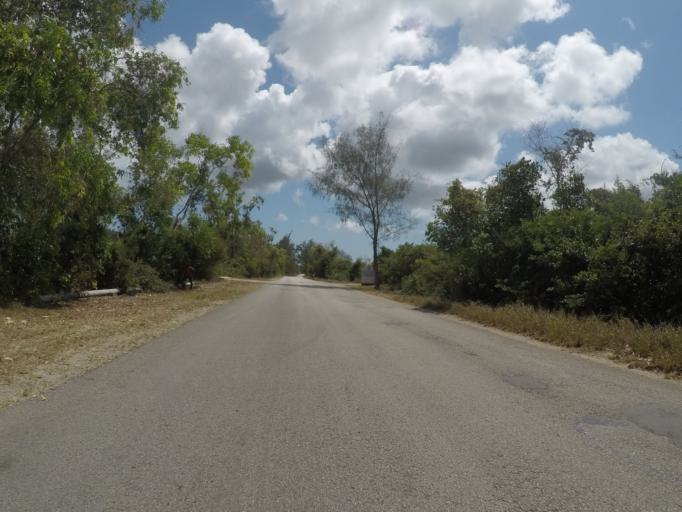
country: TZ
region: Zanzibar Central/South
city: Nganane
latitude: -6.2868
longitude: 39.4475
